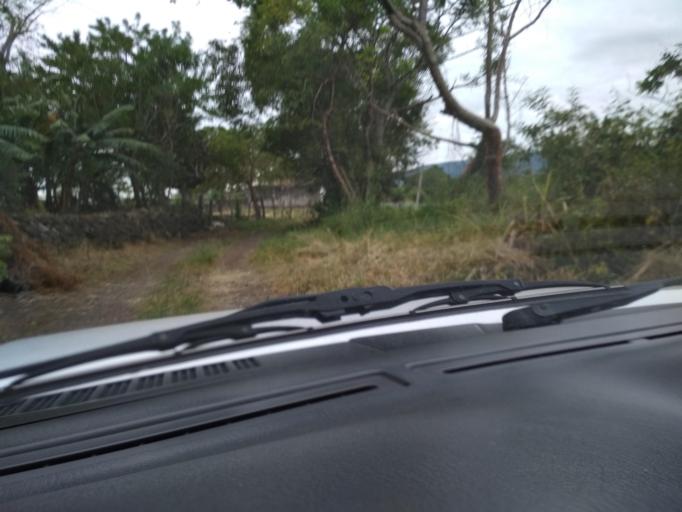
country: MX
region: Veracruz
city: Alto Lucero
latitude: 19.5958
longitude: -96.7828
